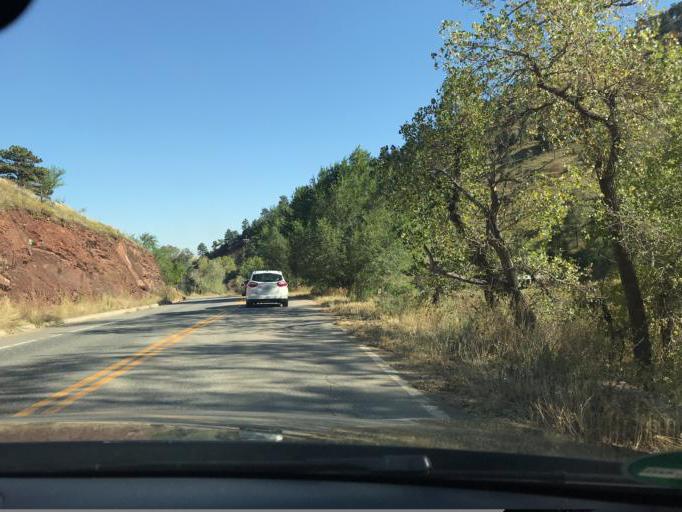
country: US
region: Colorado
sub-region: Boulder County
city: Boulder
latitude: 40.0645
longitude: -105.3002
